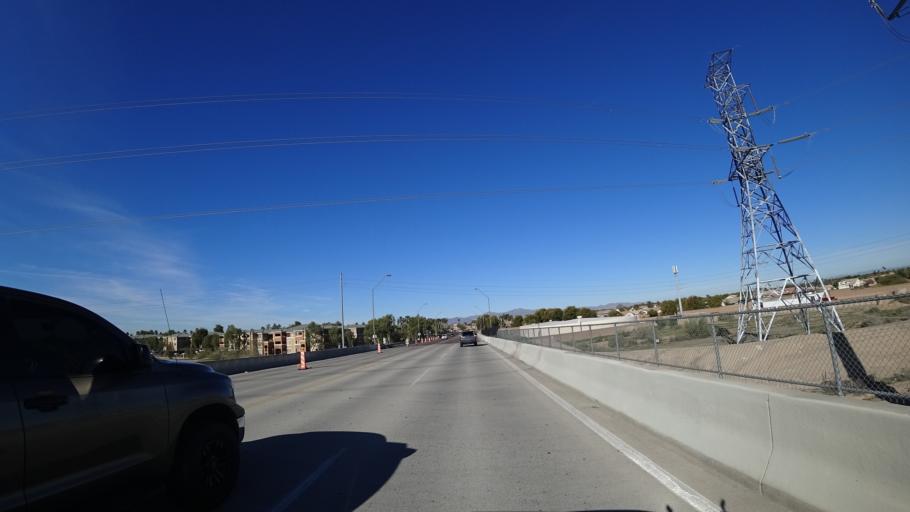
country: US
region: Arizona
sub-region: Maricopa County
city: Avondale
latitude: 33.4630
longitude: -112.3313
